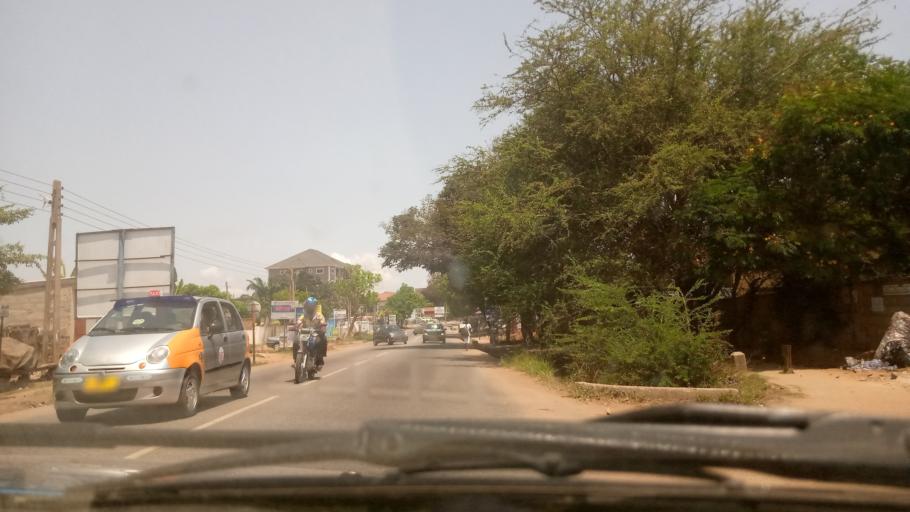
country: GH
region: Greater Accra
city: Accra
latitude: 5.5429
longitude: -0.2397
